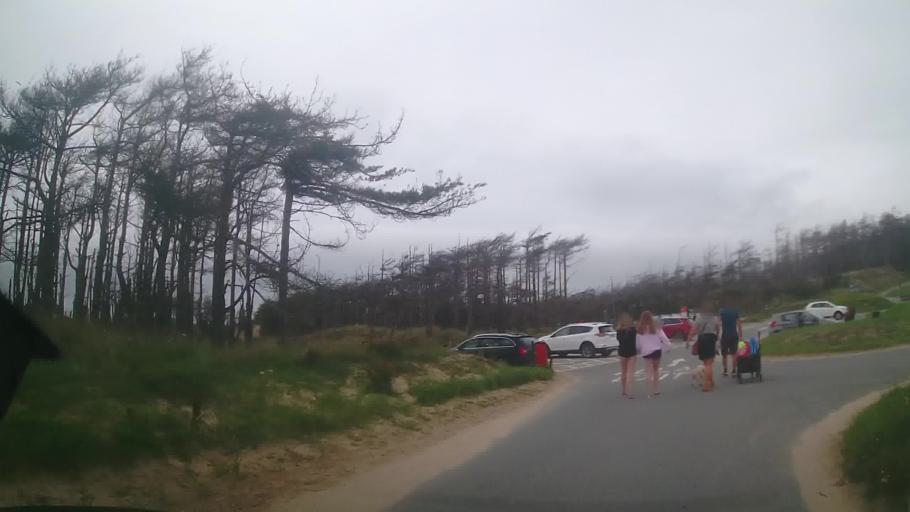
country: GB
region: Wales
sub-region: Gwynedd
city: Caernarfon
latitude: 53.1442
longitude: -4.3853
